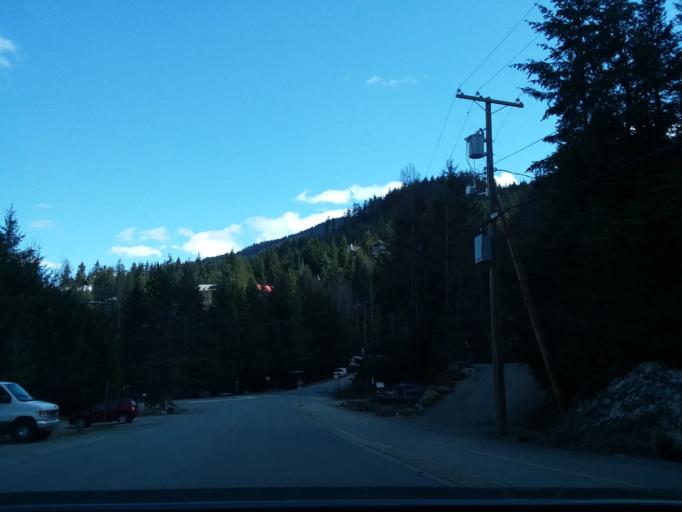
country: CA
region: British Columbia
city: Whistler
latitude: 50.0887
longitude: -123.0001
